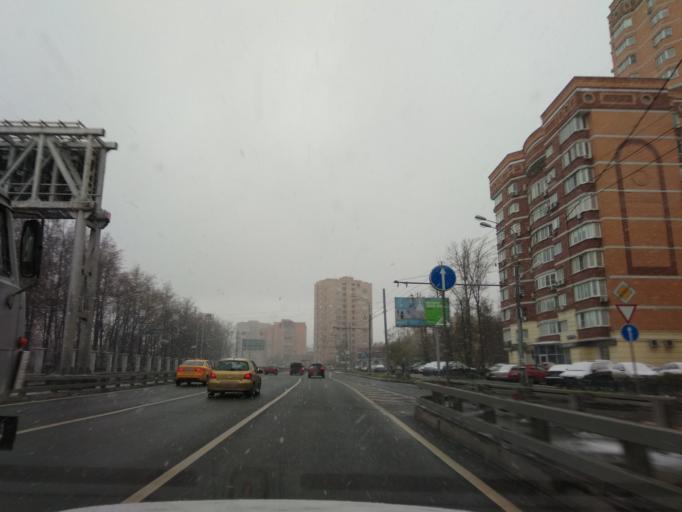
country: RU
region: Moskovskaya
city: Koptevo
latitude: 55.8350
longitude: 37.5357
